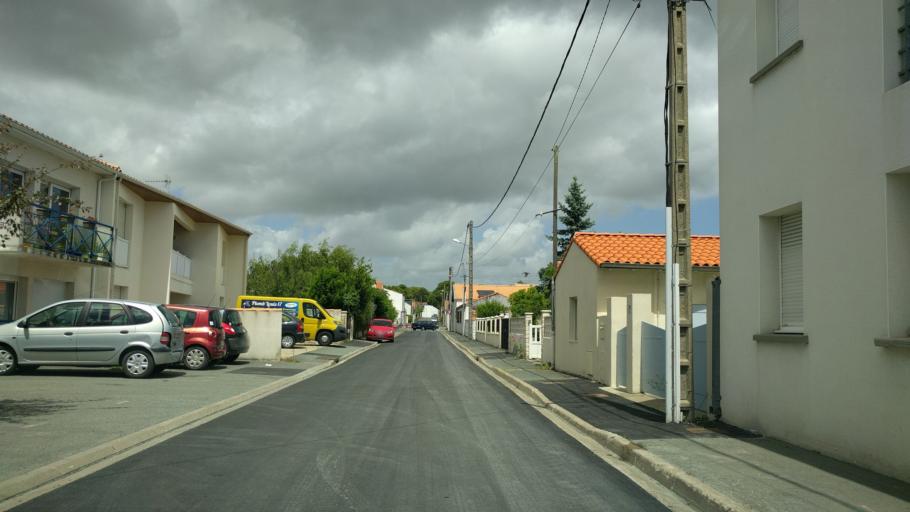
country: FR
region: Poitou-Charentes
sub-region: Departement de la Charente-Maritime
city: La Rochelle
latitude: 46.1602
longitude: -1.1354
